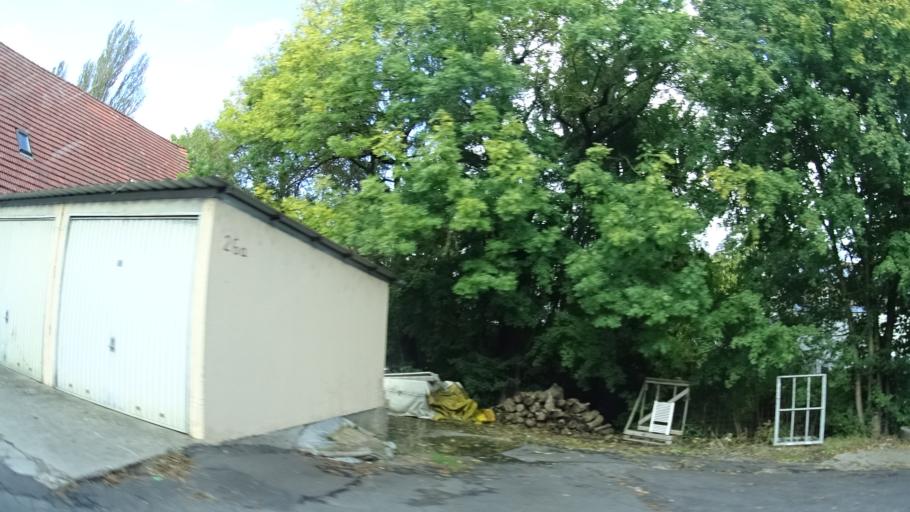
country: DE
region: Bavaria
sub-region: Regierungsbezirk Unterfranken
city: Kitzingen
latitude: 49.7372
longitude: 10.1473
